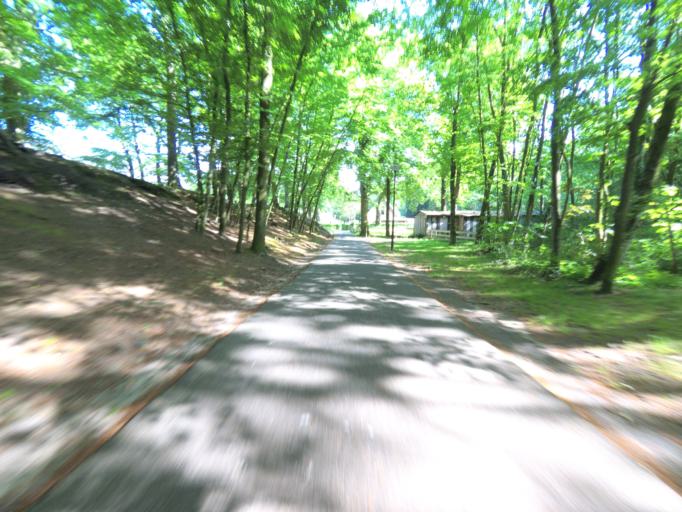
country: NL
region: Utrecht
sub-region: Gemeente Amersfoort
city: Amersfoort
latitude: 52.1394
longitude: 5.3863
